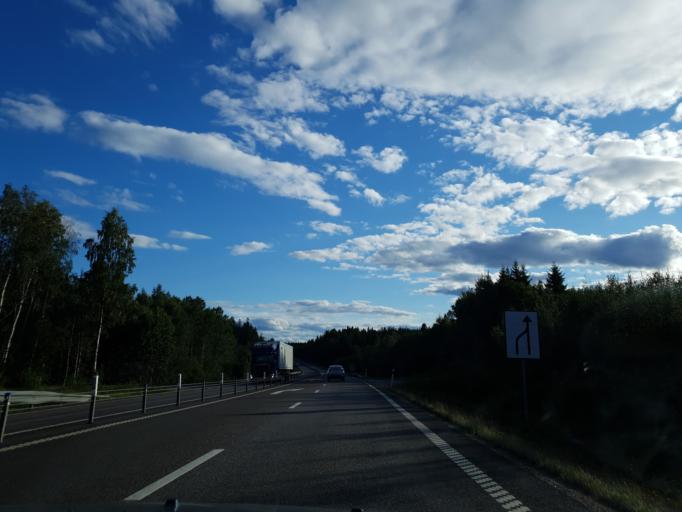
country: SE
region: Vaesternorrland
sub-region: Sundsvalls Kommun
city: Njurundabommen
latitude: 62.0730
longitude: 17.2719
